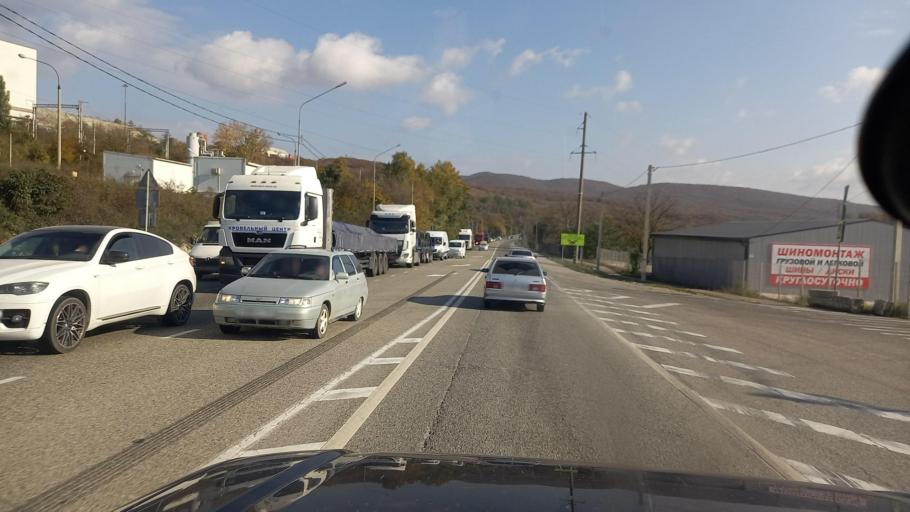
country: RU
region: Krasnodarskiy
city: Verkhnebakanskiy
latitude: 44.8425
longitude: 37.6711
